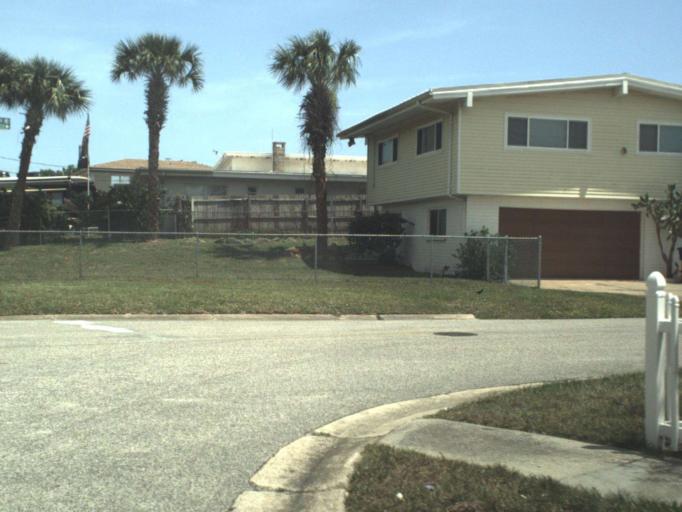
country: US
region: Florida
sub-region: Volusia County
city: Daytona Beach Shores
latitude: 29.1898
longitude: -80.9933
